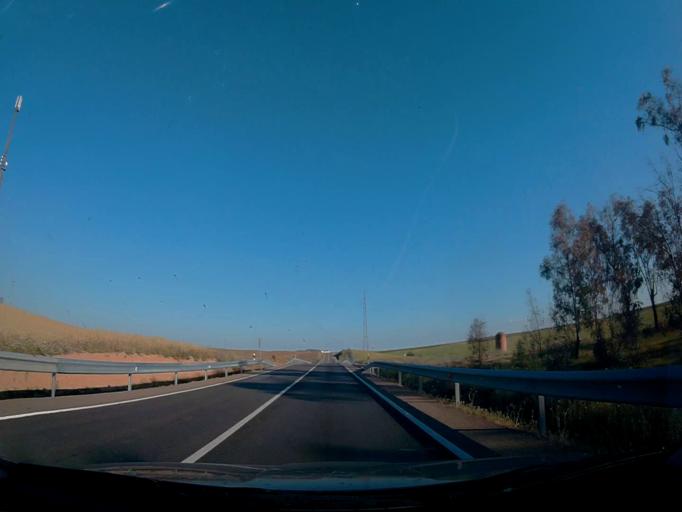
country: ES
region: Castille-La Mancha
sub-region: Province of Toledo
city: Hormigos
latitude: 40.1149
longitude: -4.4042
